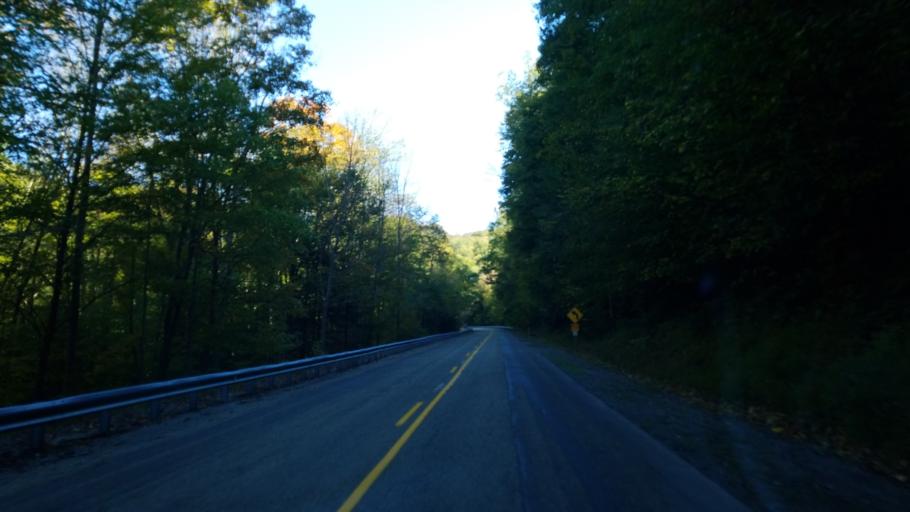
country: US
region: Pennsylvania
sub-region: Clearfield County
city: Shiloh
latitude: 41.2524
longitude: -78.3813
